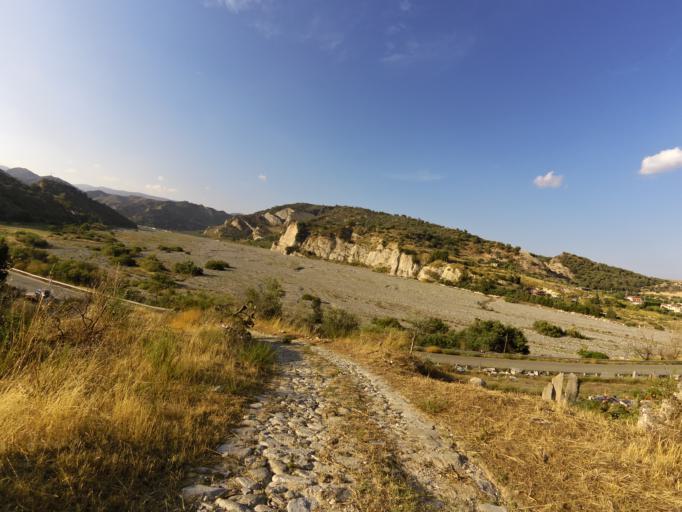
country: IT
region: Calabria
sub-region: Provincia di Reggio Calabria
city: Stilo
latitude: 38.4650
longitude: 16.4877
